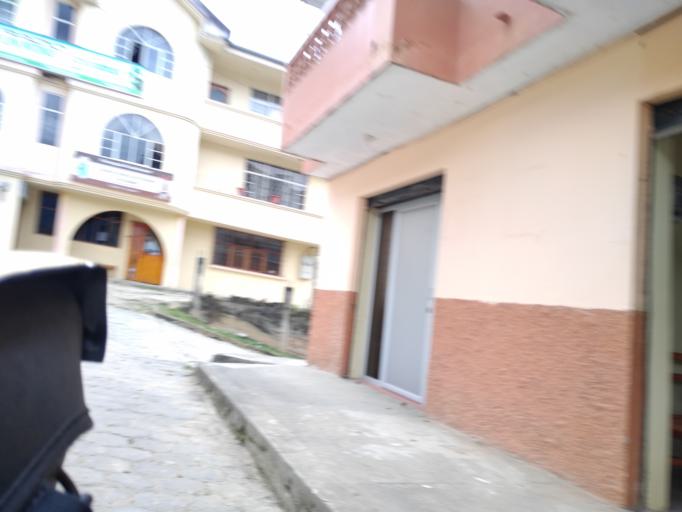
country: PE
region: Cajamarca
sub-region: Provincia de San Ignacio
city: Namballe
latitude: -4.8636
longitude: -79.1308
